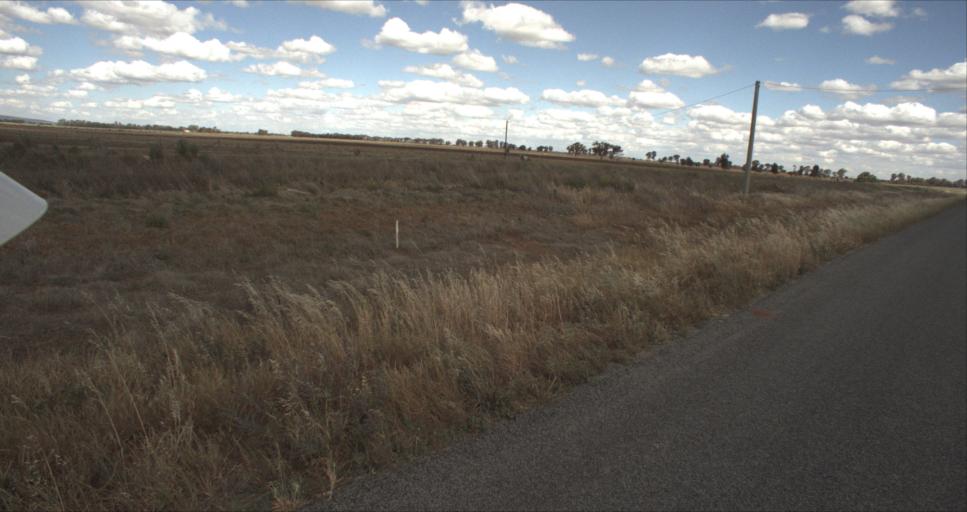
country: AU
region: New South Wales
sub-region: Leeton
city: Leeton
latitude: -34.4496
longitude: 146.2548
